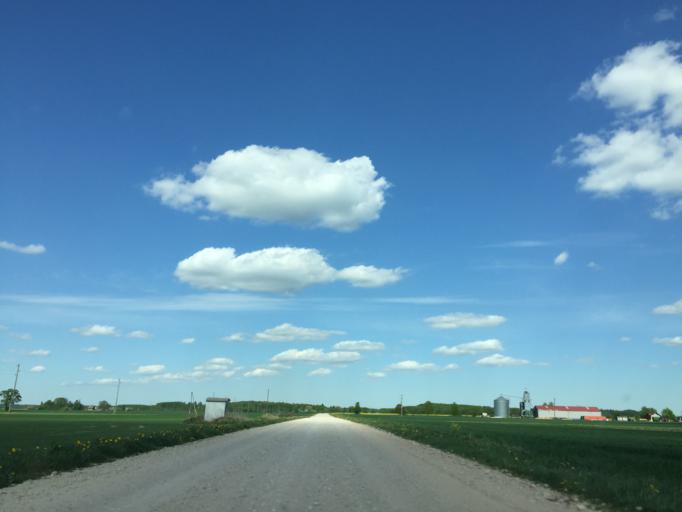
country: LV
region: Rundales
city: Pilsrundale
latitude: 56.3604
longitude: 24.0258
